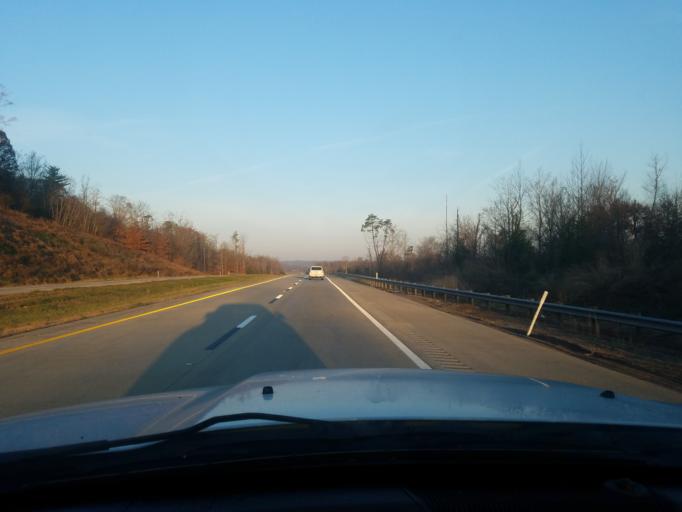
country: US
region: West Virginia
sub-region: Putnam County
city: Eleanor
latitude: 38.5353
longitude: -81.9567
